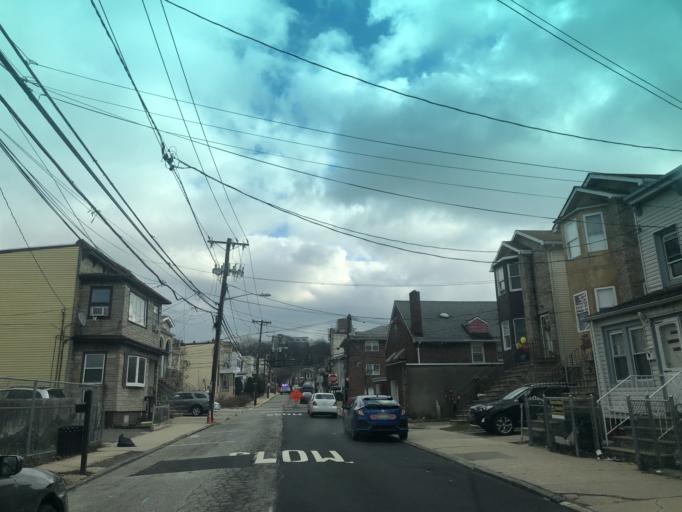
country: US
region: New Jersey
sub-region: Hudson County
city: Union City
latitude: 40.7853
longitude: -74.0303
